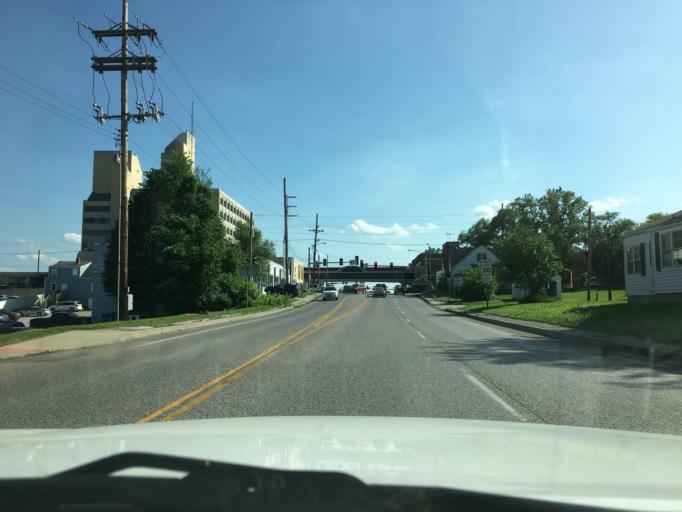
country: US
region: Missouri
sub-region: Franklin County
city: Washington
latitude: 38.5541
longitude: -91.0007
